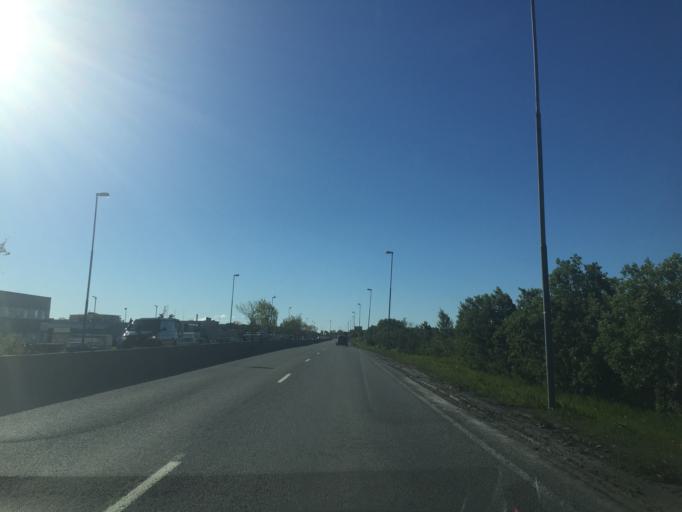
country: NO
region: Nordland
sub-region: Bodo
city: Bodo
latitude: 67.2791
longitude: 14.4294
